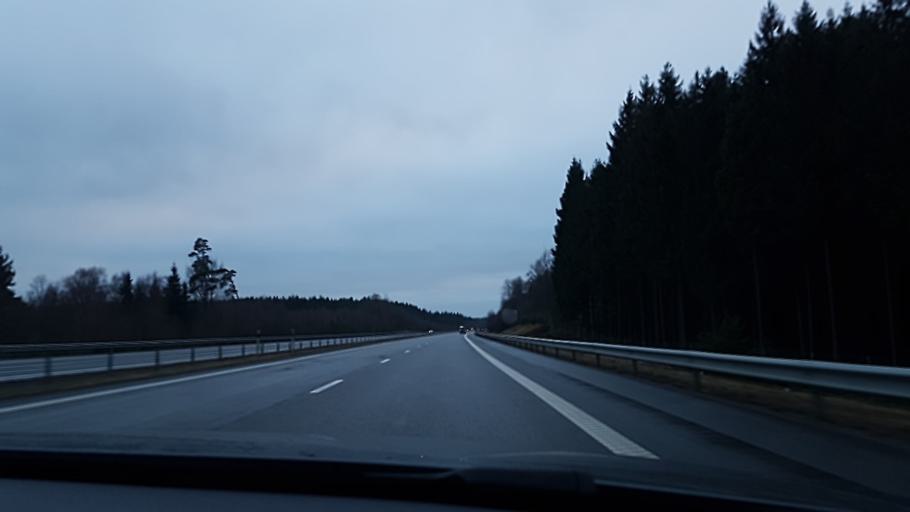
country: SE
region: Skane
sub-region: Klippans Kommun
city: Klippan
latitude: 56.2202
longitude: 13.1360
